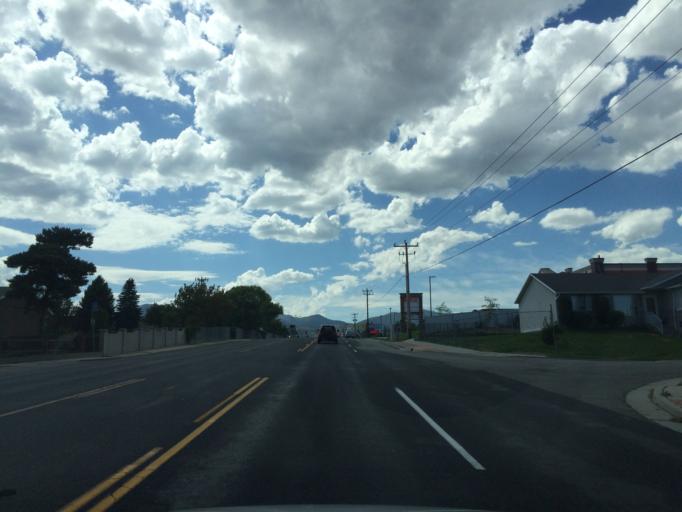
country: US
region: Utah
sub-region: Salt Lake County
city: Oquirrh
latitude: 40.6386
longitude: -112.0212
